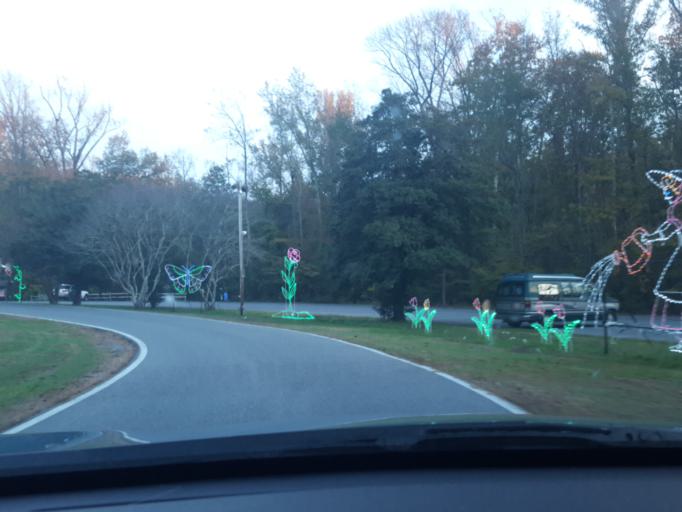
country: US
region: Maryland
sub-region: Prince George's County
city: Kettering
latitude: 38.8878
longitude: -76.7985
